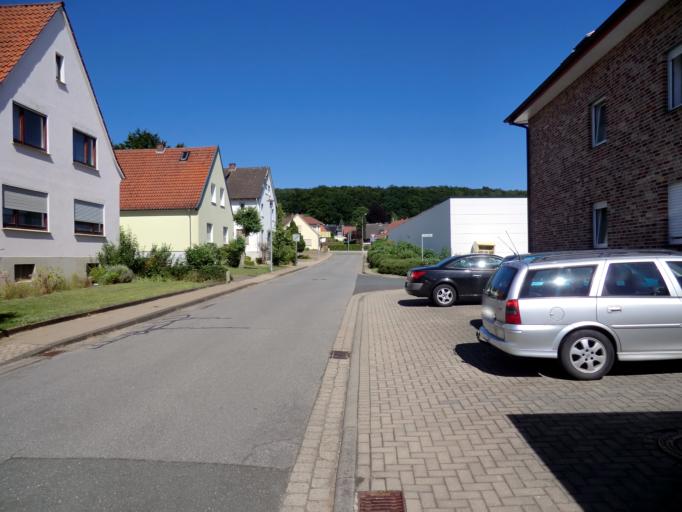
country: DE
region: North Rhine-Westphalia
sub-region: Regierungsbezirk Detmold
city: Hiddenhausen
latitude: 52.1533
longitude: 8.6432
